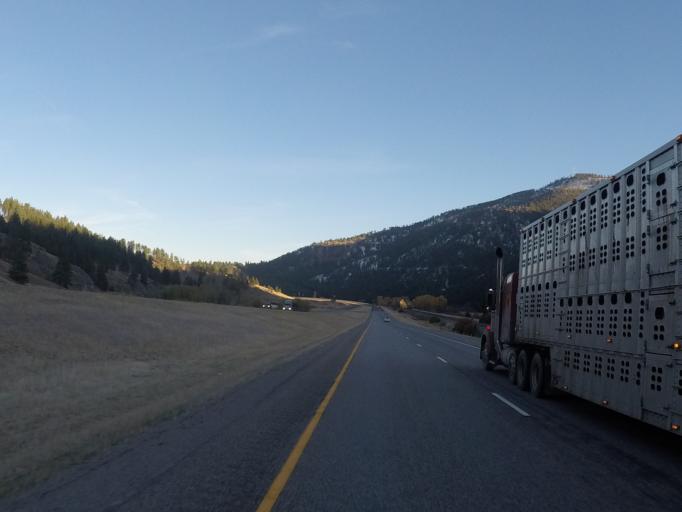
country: US
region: Montana
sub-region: Missoula County
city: Clinton
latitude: 46.7037
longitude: -113.5015
